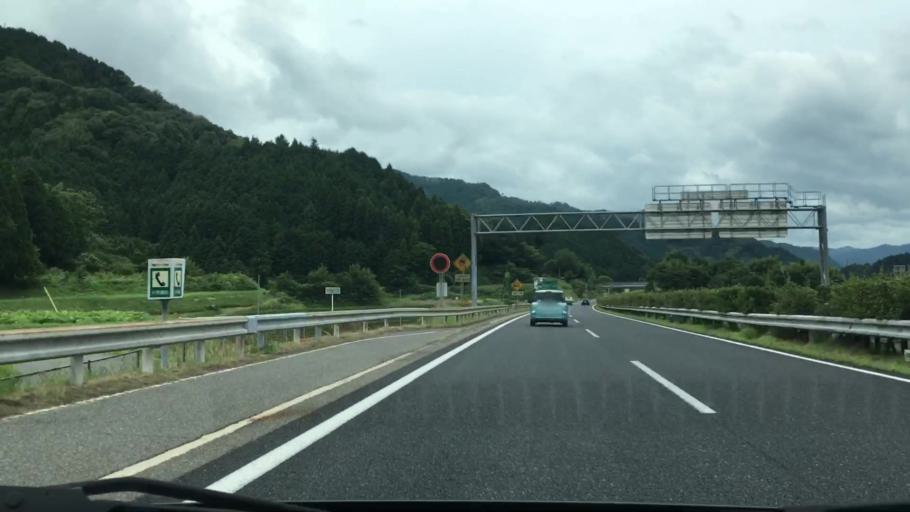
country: JP
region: Okayama
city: Tsuyama
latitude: 35.0435
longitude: 133.7986
